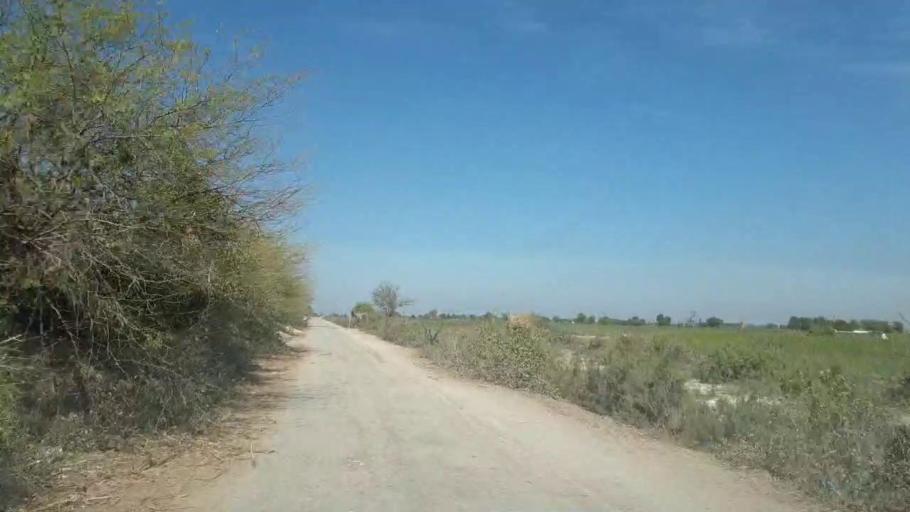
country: PK
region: Sindh
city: Pithoro
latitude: 25.6099
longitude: 69.2166
